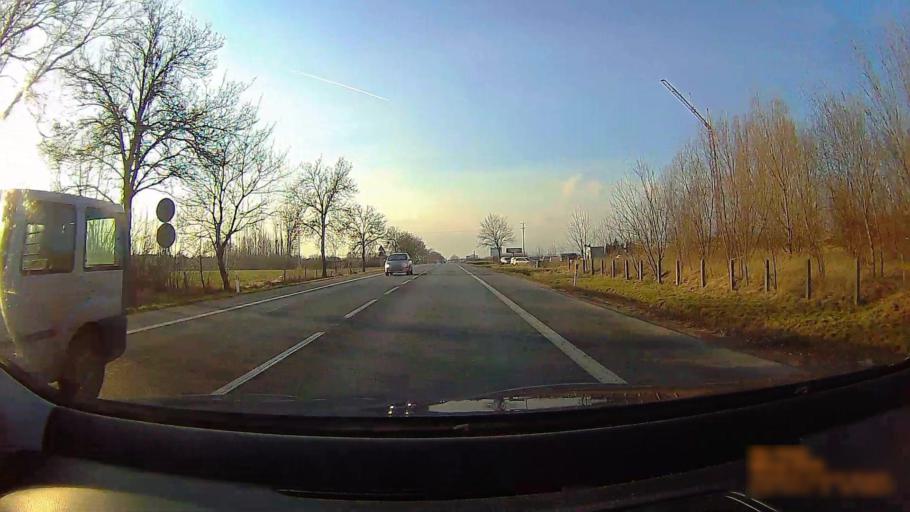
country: PL
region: Greater Poland Voivodeship
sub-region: Konin
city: Konin
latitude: 52.1911
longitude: 18.3307
